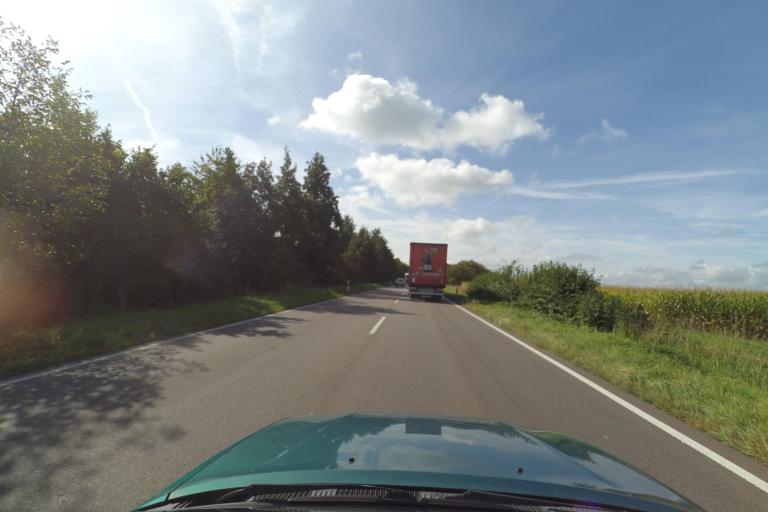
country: DE
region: Baden-Wuerttemberg
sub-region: Freiburg Region
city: Achern
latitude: 48.6424
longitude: 8.0760
